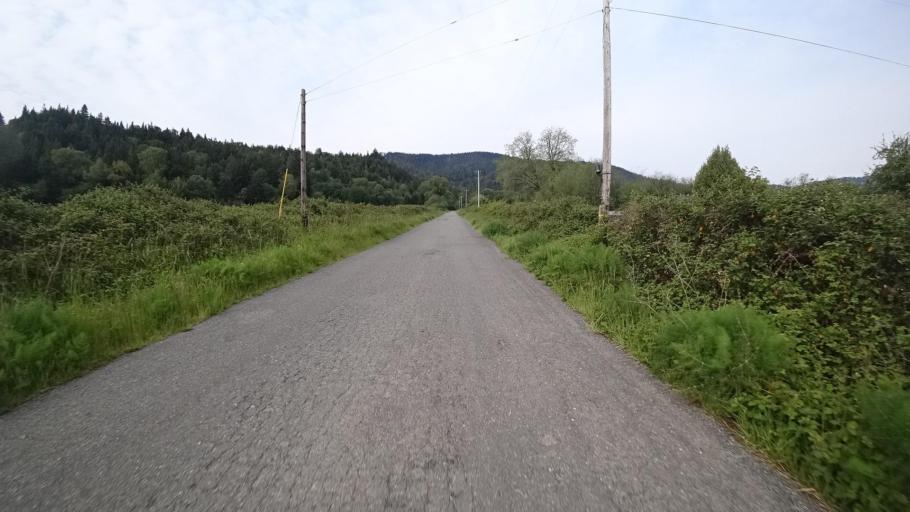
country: US
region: California
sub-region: Humboldt County
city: Redway
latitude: 40.3426
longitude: -123.8915
